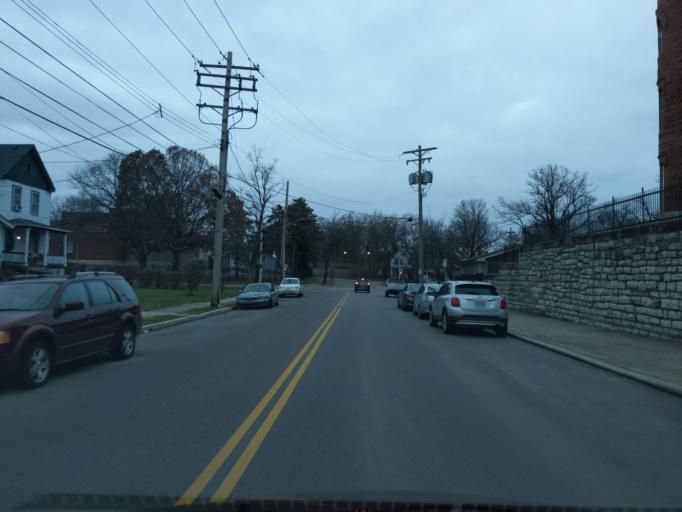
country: US
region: Kentucky
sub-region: Campbell County
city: Dayton
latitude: 39.1284
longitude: -84.4828
